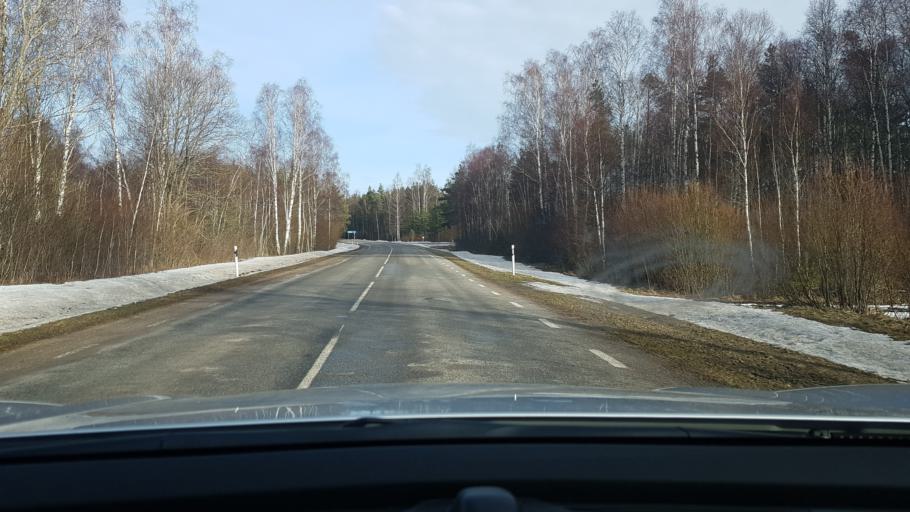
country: EE
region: Saare
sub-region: Kuressaare linn
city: Kuressaare
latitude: 58.4875
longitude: 22.7085
